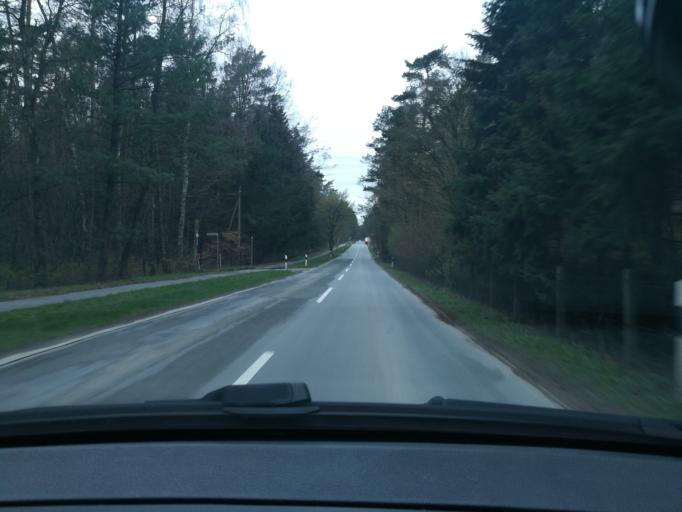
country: DE
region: North Rhine-Westphalia
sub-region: Regierungsbezirk Detmold
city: Oerlinghausen
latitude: 51.9505
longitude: 8.6226
